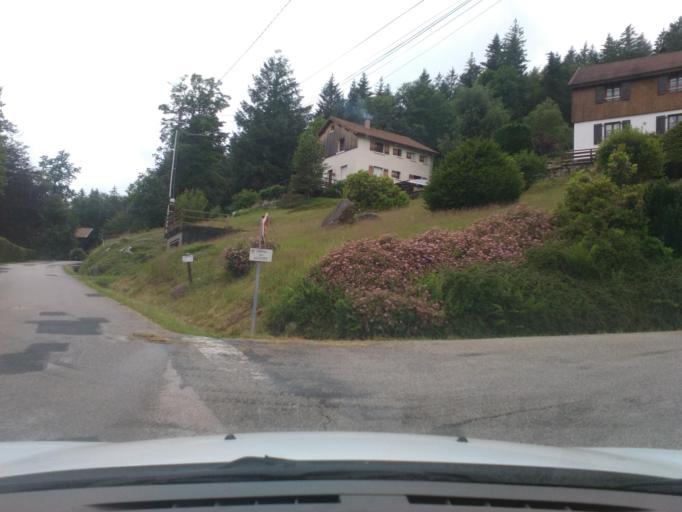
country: FR
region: Lorraine
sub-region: Departement des Vosges
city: Gerardmer
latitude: 48.0760
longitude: 6.8576
